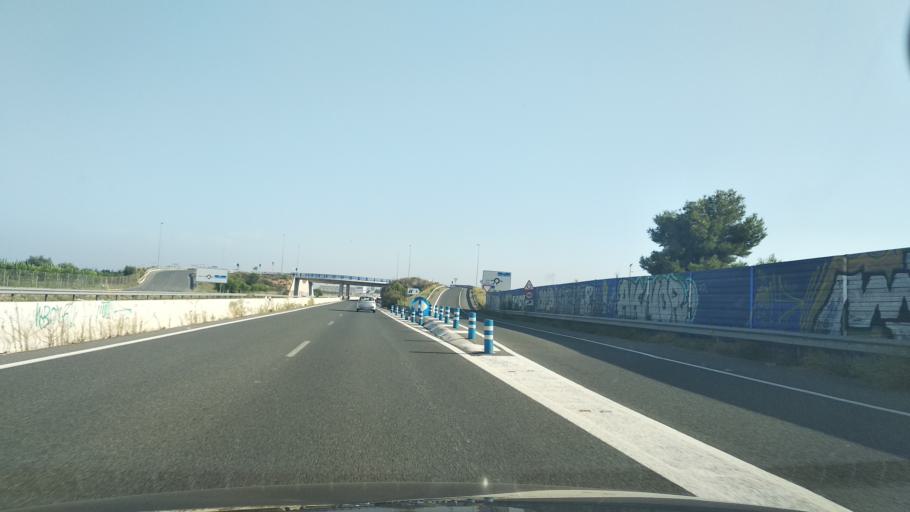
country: ES
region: Murcia
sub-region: Murcia
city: San Javier
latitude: 37.8510
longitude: -0.8792
